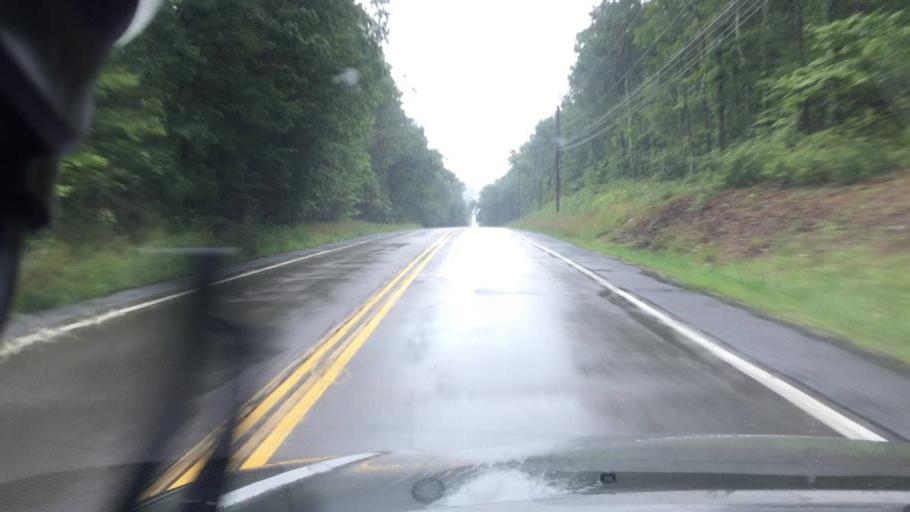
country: US
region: Pennsylvania
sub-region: Luzerne County
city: Freeland
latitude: 41.0266
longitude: -75.8606
